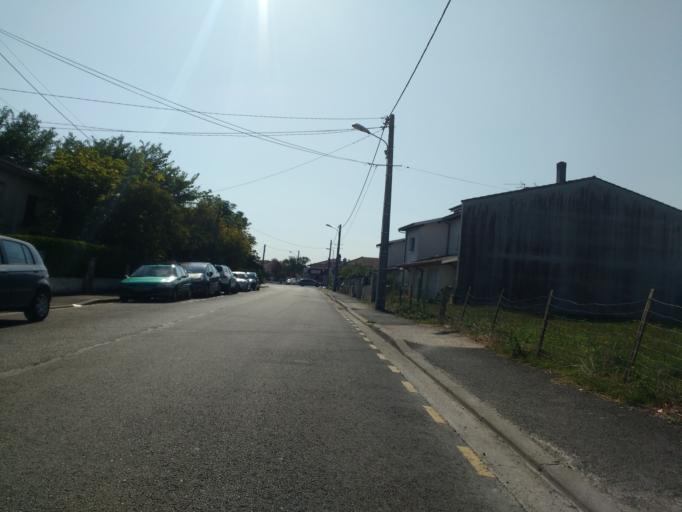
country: FR
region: Aquitaine
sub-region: Departement de la Gironde
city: Pessac
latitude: 44.8104
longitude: -0.6272
